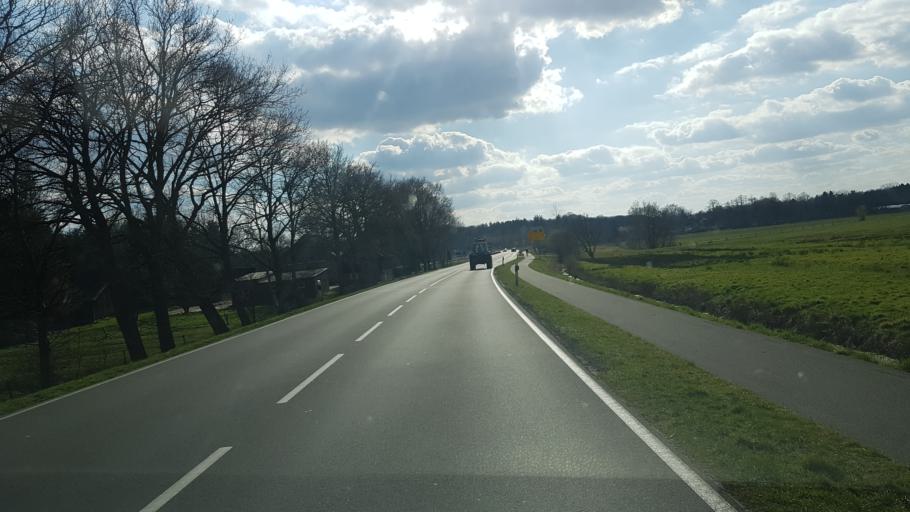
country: DE
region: Lower Saxony
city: Rastede
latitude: 53.2364
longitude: 8.2800
